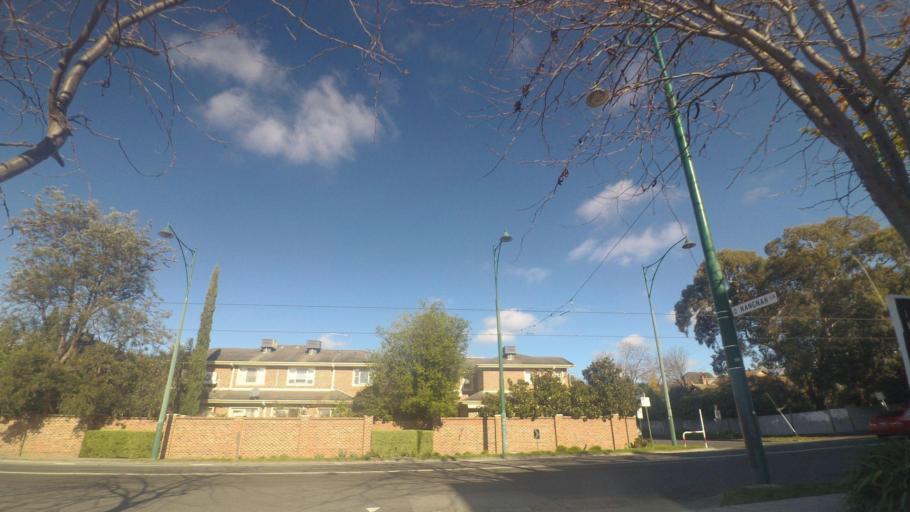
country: AU
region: Victoria
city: Mont Albert
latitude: -37.8162
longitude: 145.1104
